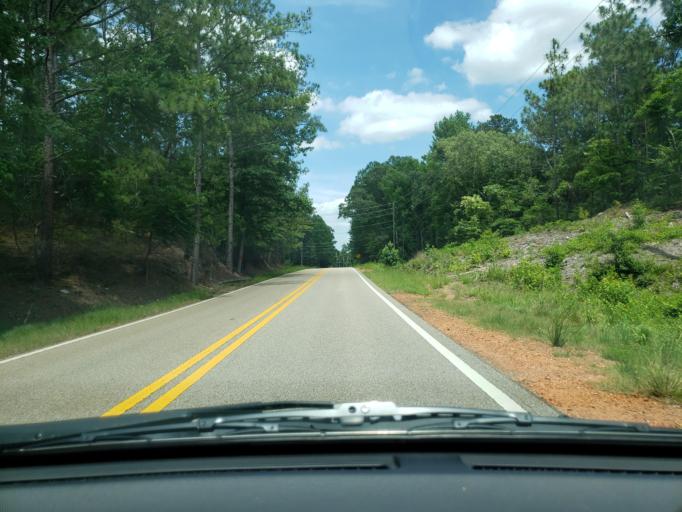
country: US
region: Alabama
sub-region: Elmore County
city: Eclectic
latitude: 32.6720
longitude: -85.9194
